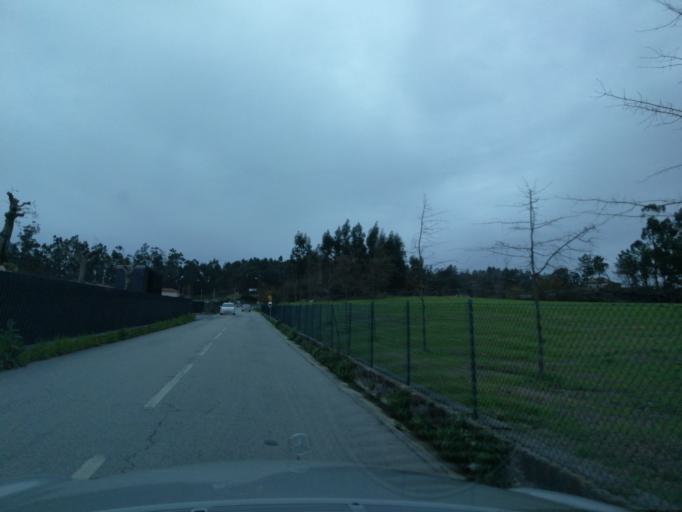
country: PT
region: Braga
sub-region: Braga
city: Oliveira
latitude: 41.4860
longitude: -8.4724
